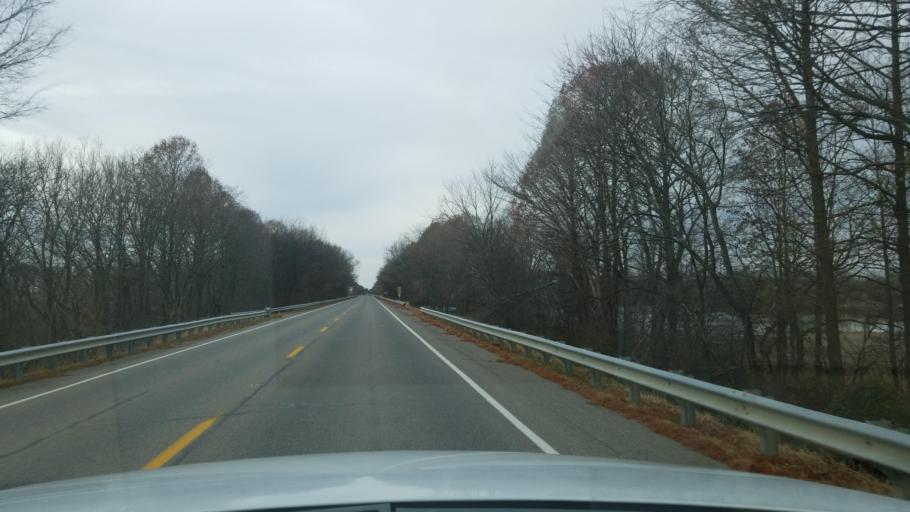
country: US
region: Indiana
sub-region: Posey County
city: Mount Vernon
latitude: 37.9290
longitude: -87.9762
